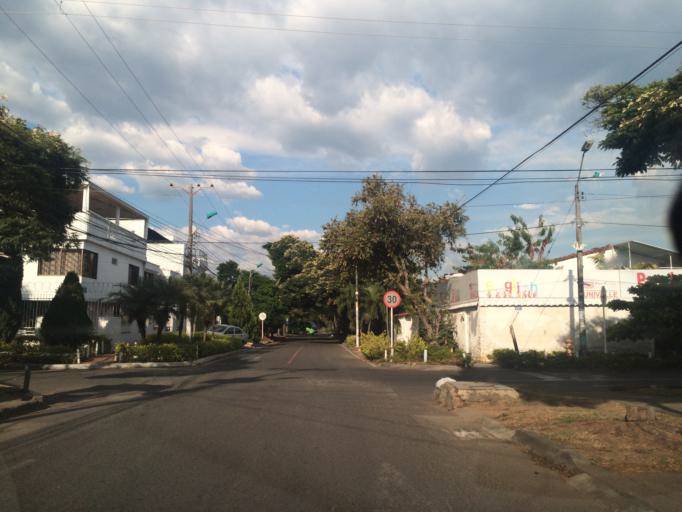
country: CO
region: Valle del Cauca
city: Cali
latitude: 3.3952
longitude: -76.5542
